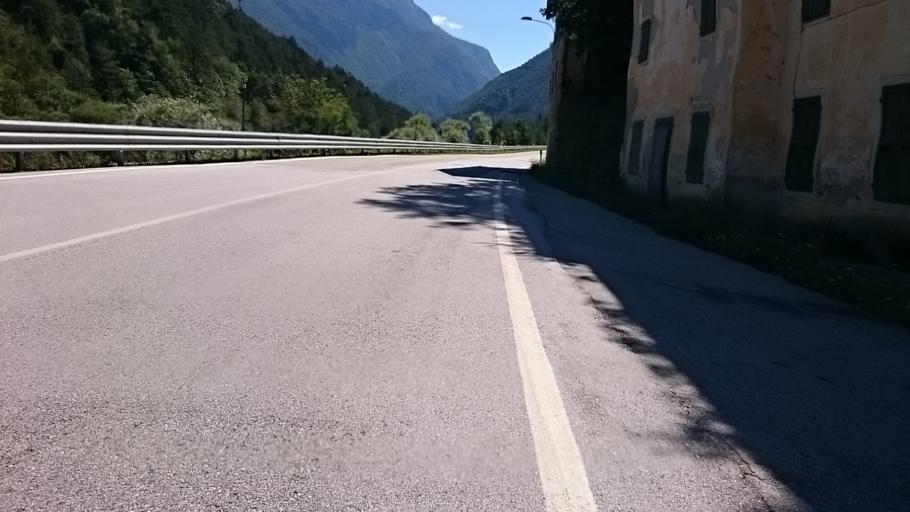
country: IT
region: Veneto
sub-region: Provincia di Belluno
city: Perarolo di Cadore
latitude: 46.3929
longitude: 12.3558
